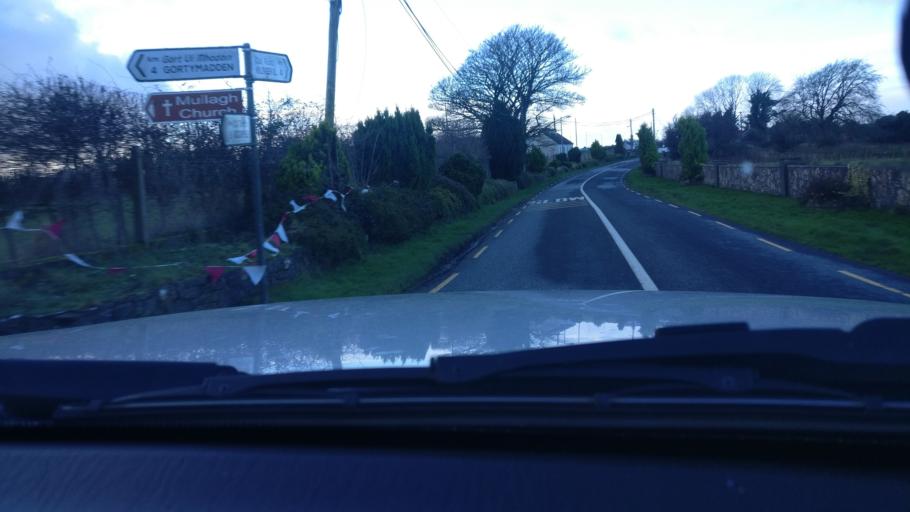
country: IE
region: Connaught
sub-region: County Galway
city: Loughrea
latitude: 53.2237
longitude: -8.3941
